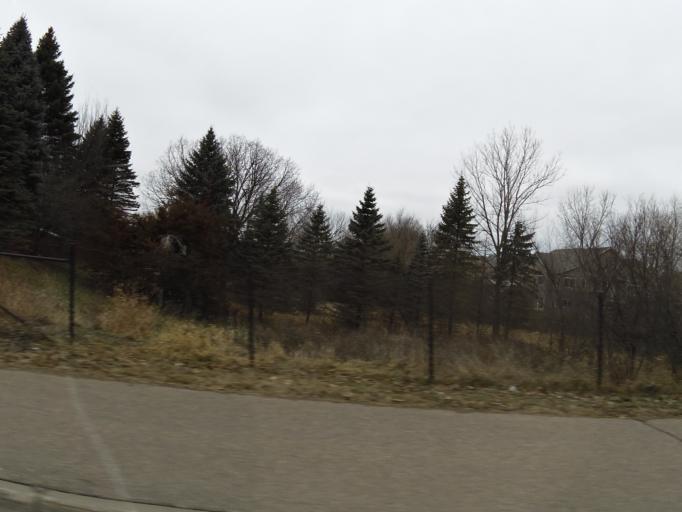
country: US
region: Minnesota
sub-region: Scott County
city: Prior Lake
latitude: 44.7260
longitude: -93.4396
